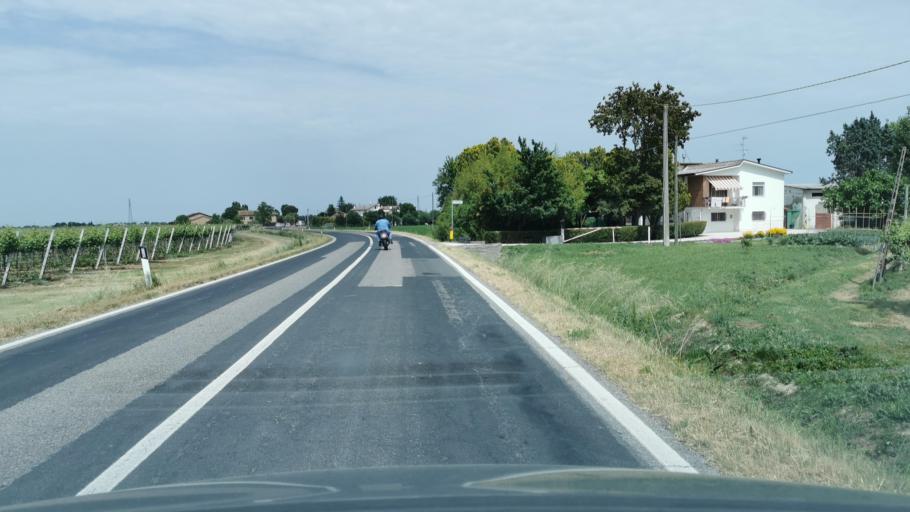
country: IT
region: Emilia-Romagna
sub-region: Provincia di Ravenna
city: Glorie
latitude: 44.4917
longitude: 12.0736
